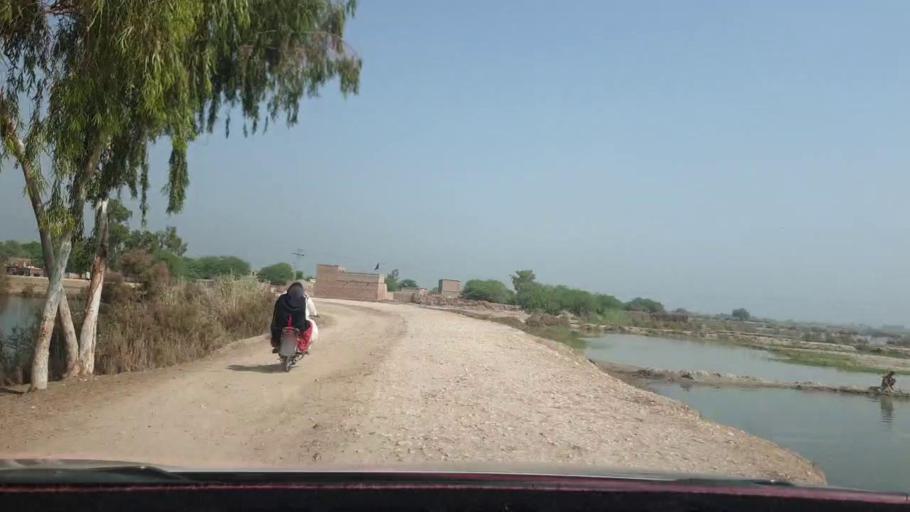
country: PK
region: Sindh
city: Nasirabad
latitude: 27.4239
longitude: 67.9283
